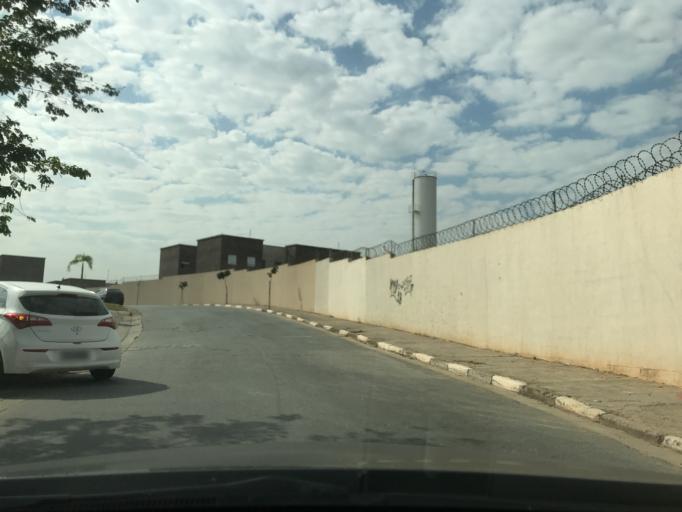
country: BR
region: Sao Paulo
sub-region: Cotia
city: Cotia
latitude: -23.6168
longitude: -46.9277
